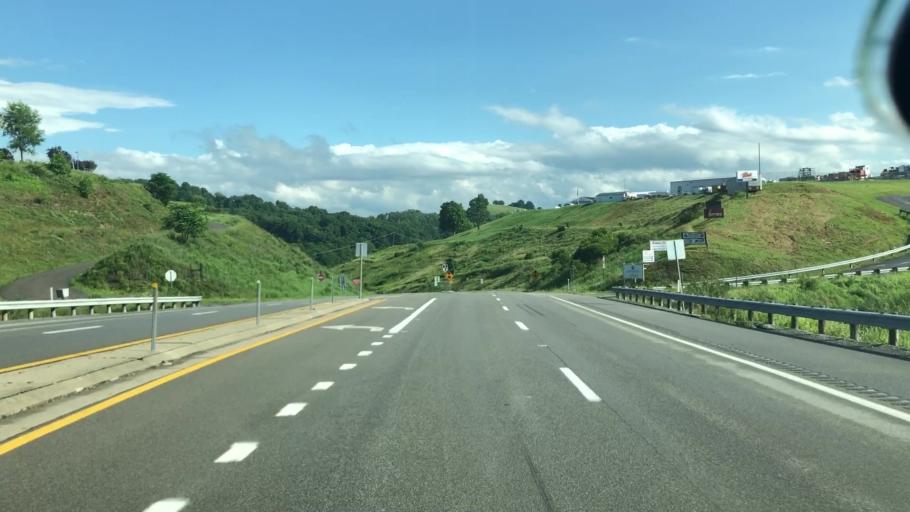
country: US
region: West Virginia
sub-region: Harrison County
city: Bridgeport
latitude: 39.3015
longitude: -80.2072
